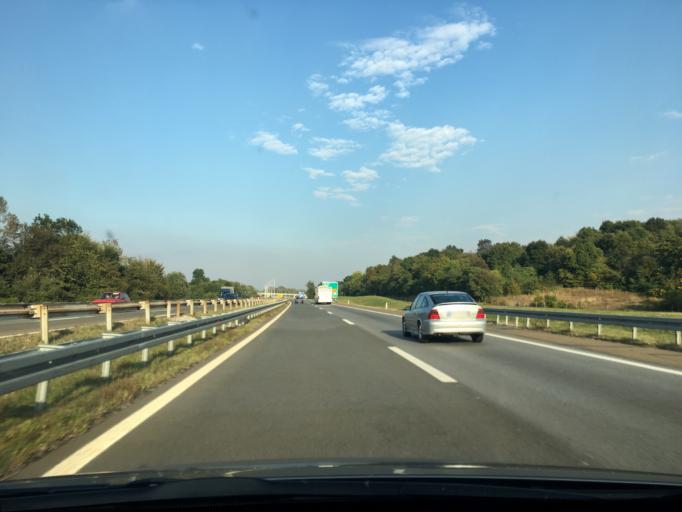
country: RS
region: Central Serbia
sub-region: Podunavski Okrug
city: Smederevo
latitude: 44.5804
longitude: 20.9487
